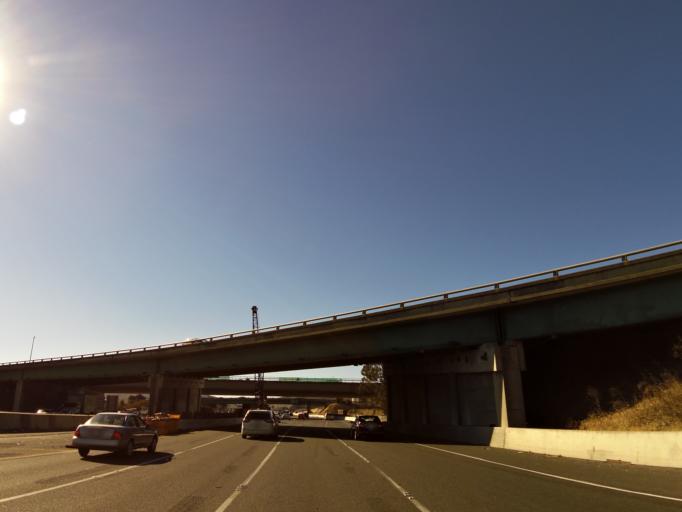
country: US
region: California
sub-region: Solano County
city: Green Valley
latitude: 38.2172
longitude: -122.1374
